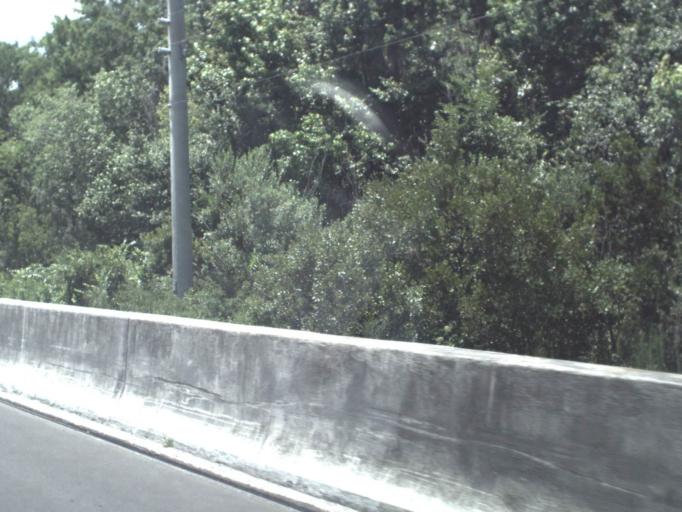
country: US
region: Florida
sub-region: Putnam County
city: East Palatka
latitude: 29.7144
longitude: -81.5154
